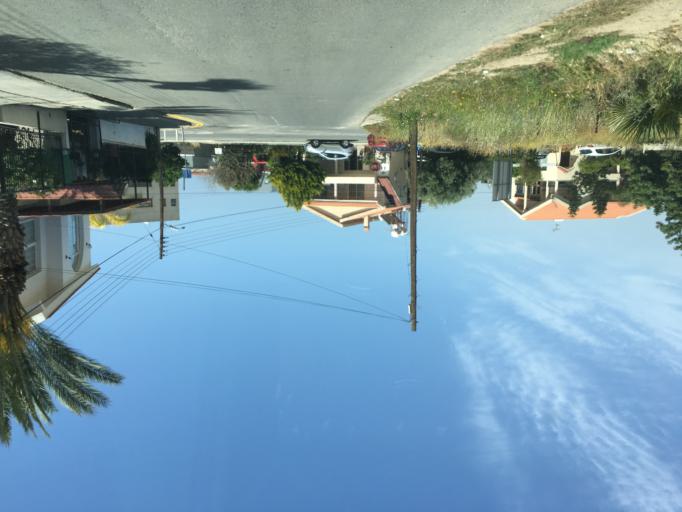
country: CY
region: Limassol
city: Mouttagiaka
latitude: 34.7045
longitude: 33.0812
